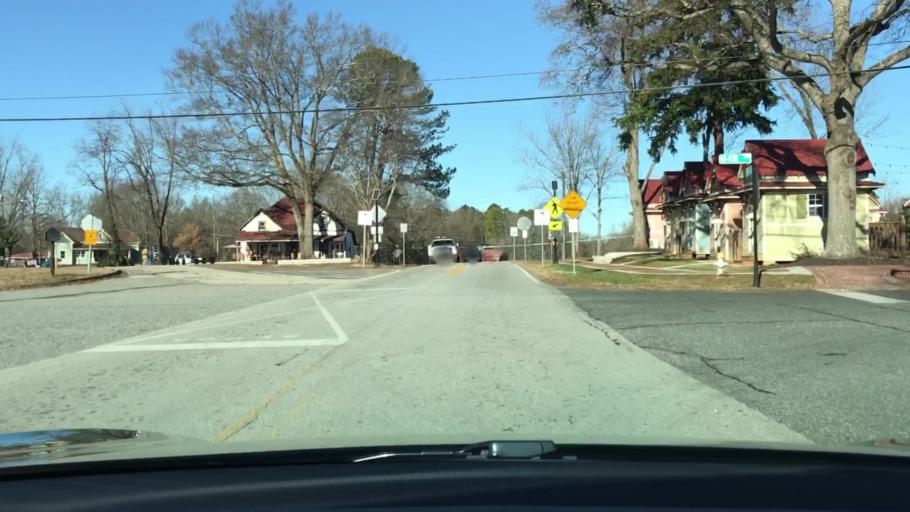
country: US
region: Georgia
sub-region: Barrow County
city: Auburn
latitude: 34.0136
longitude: -83.8280
